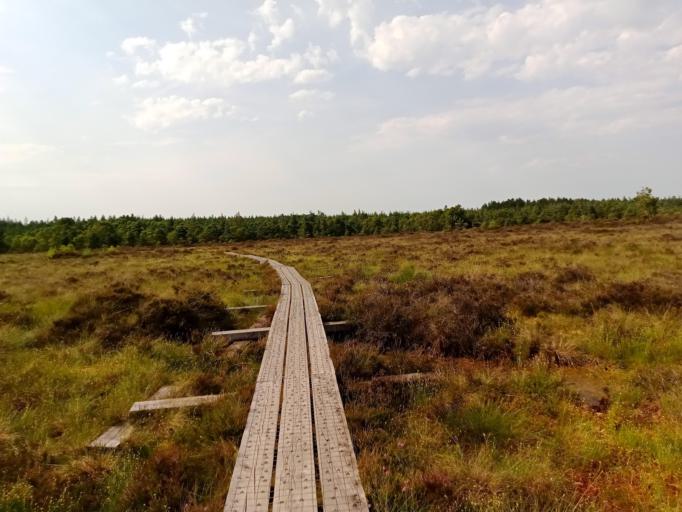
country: IE
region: Leinster
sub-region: Laois
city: Abbeyleix
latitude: 52.8936
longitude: -7.3544
